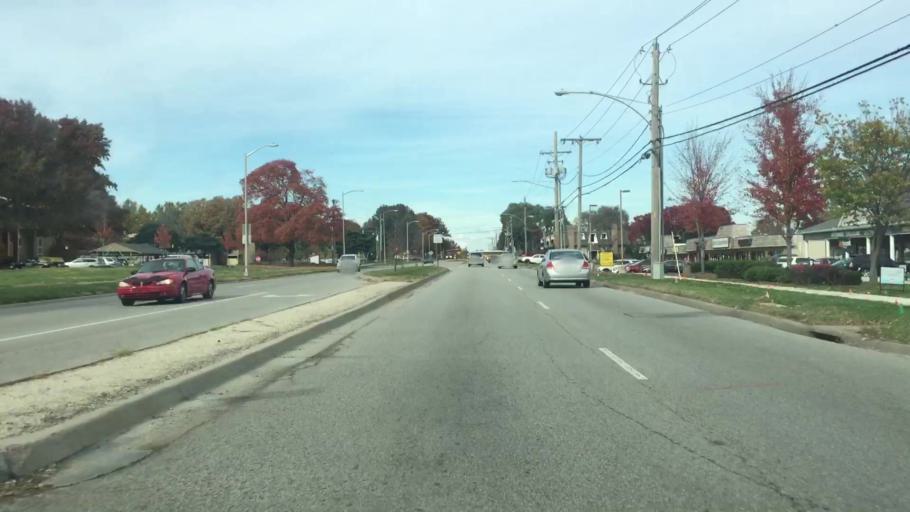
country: US
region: Kansas
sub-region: Johnson County
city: Lenexa
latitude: 38.9880
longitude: -94.7236
